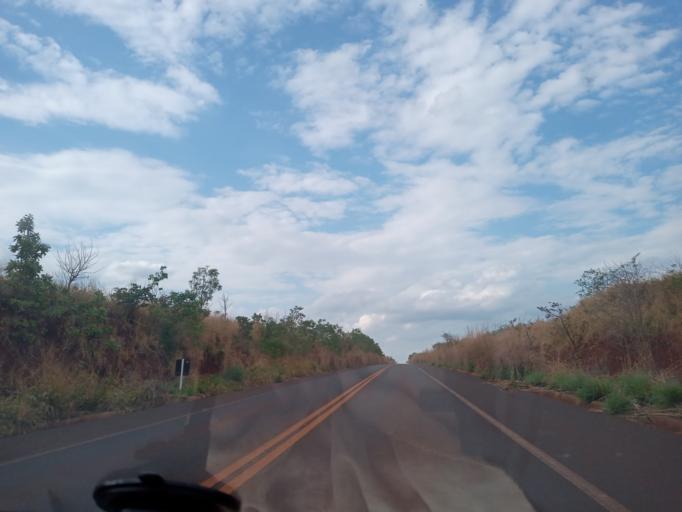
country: BR
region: Minas Gerais
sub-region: Ituiutaba
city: Ituiutaba
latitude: -19.1134
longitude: -49.5194
